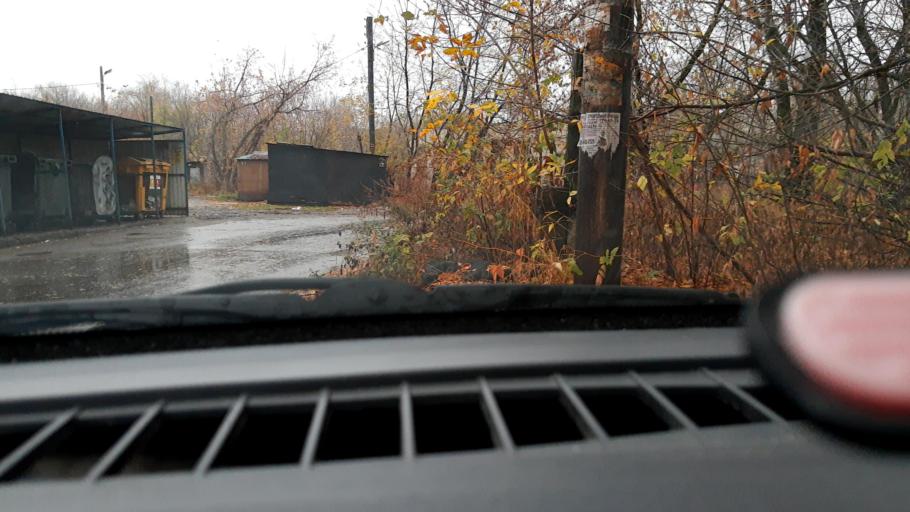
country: RU
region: Nizjnij Novgorod
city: Nizhniy Novgorod
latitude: 56.3019
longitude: 43.9119
